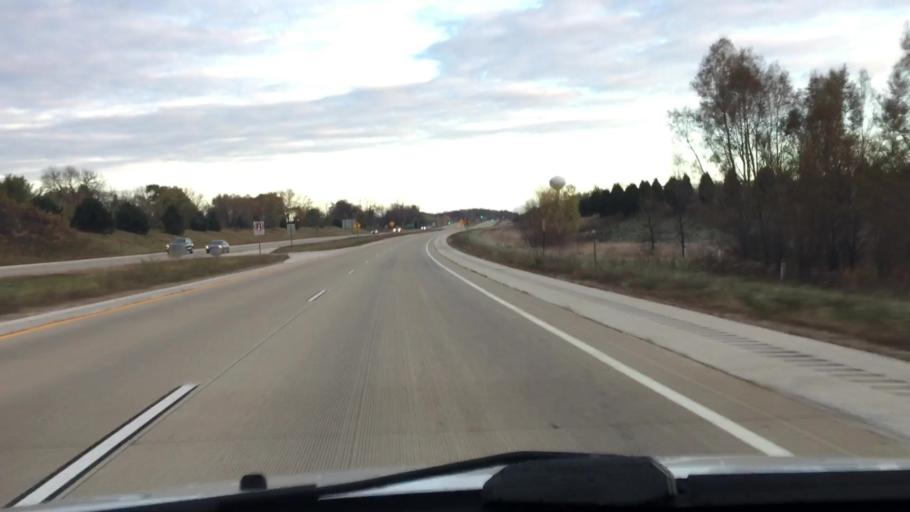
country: US
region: Wisconsin
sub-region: Waukesha County
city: Oconomowoc
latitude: 43.1169
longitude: -88.4797
